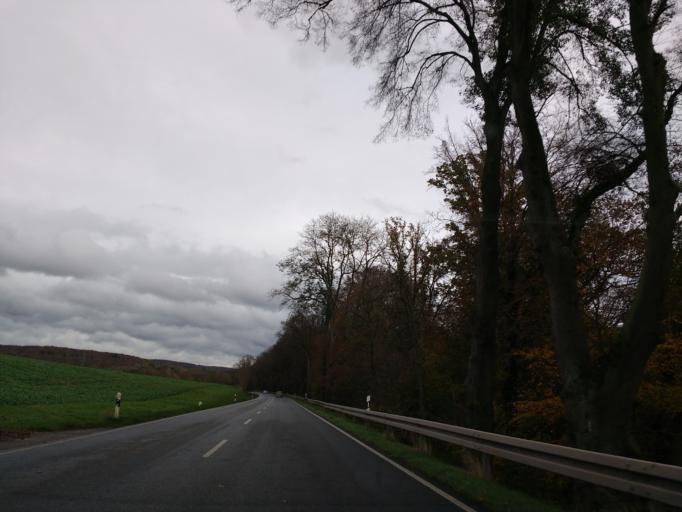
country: DE
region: Hesse
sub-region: Regierungsbezirk Kassel
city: Sachsenhausen
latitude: 51.2378
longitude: 9.0419
